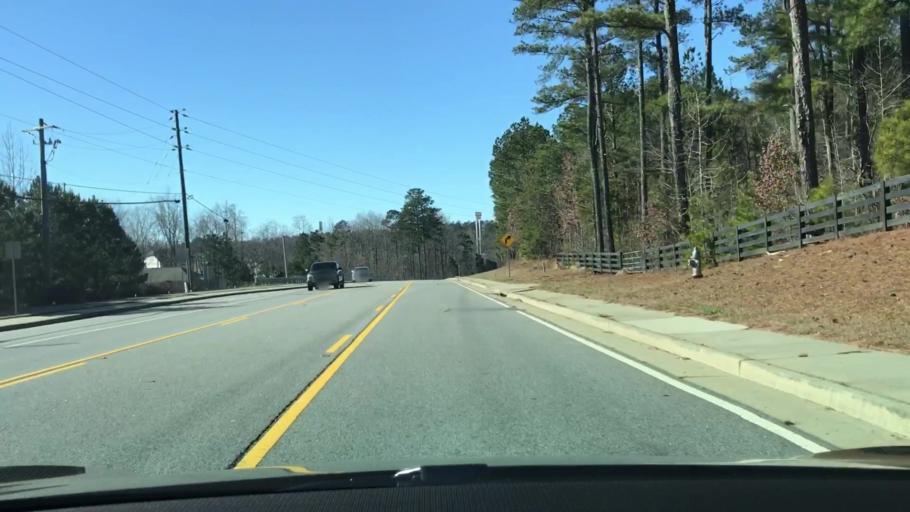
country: US
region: Georgia
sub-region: Forsyth County
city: Cumming
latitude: 34.1872
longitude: -84.1258
